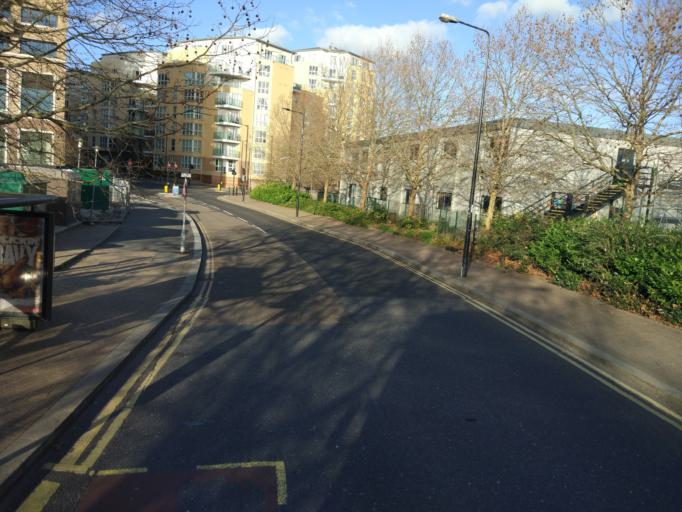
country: GB
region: England
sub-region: Greater London
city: Poplar
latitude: 51.4975
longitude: -0.0458
